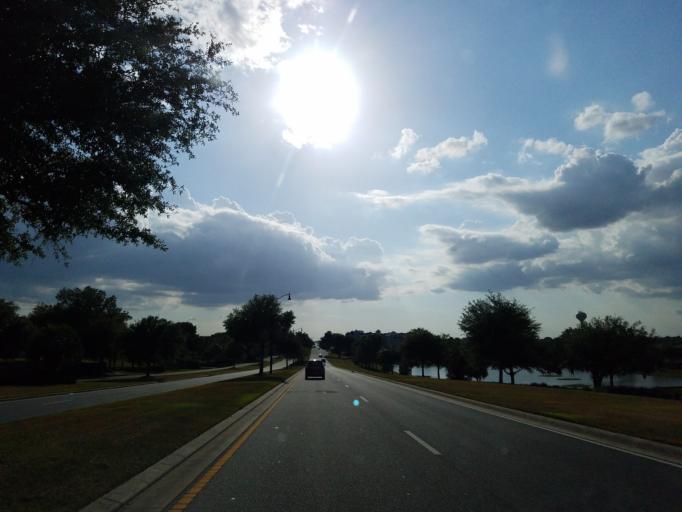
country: US
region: Florida
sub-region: Sumter County
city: Wildwood
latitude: 28.8654
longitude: -81.9834
